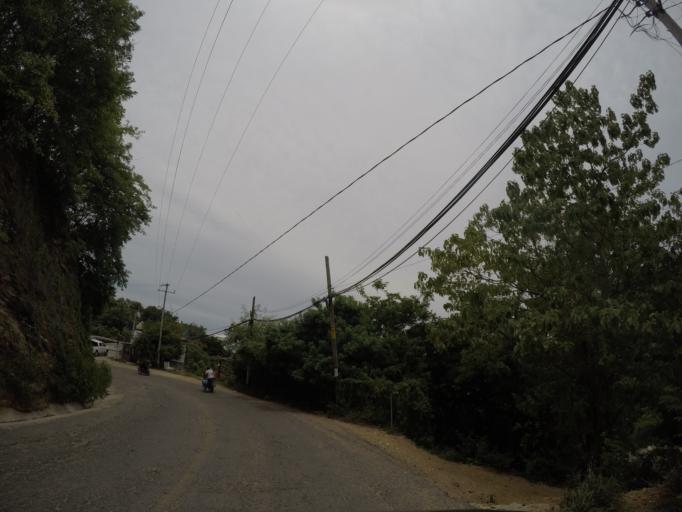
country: MX
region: Oaxaca
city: San Pedro Pochutla
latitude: 15.6670
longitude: -96.4961
